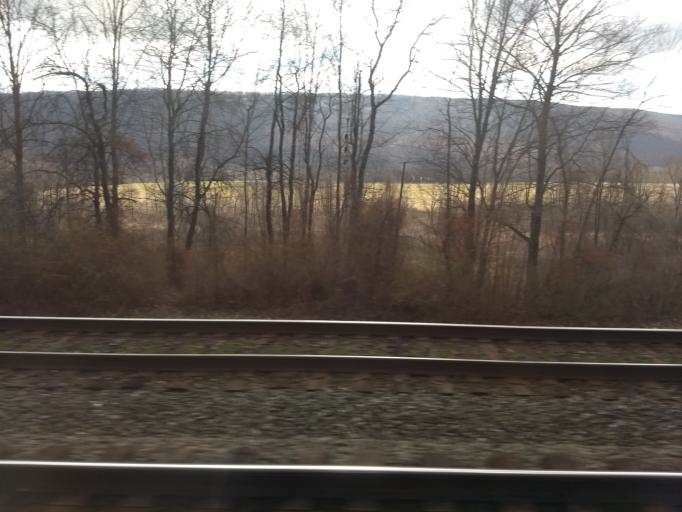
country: US
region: Pennsylvania
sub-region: Blair County
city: Bellwood
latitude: 40.6129
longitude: -78.3233
